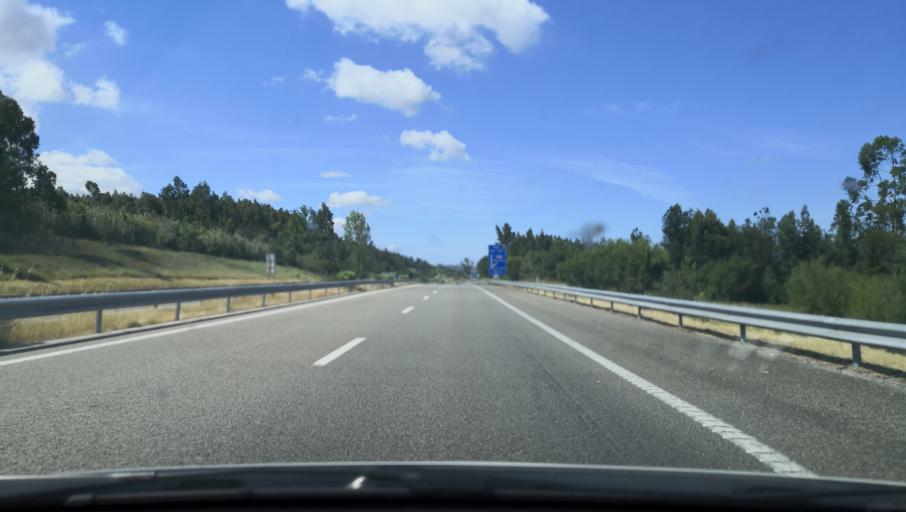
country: PT
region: Coimbra
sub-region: Montemor-O-Velho
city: Montemor-o-Velho
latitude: 40.1821
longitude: -8.7041
